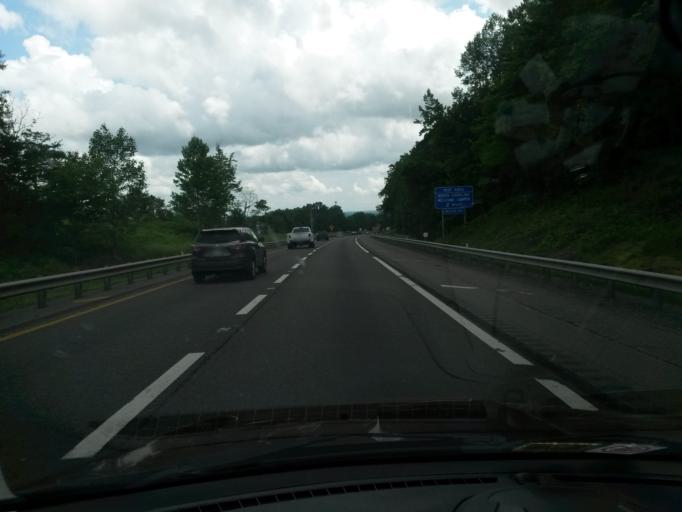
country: US
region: Virginia
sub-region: Carroll County
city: Cana
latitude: 36.5903
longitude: -80.7423
